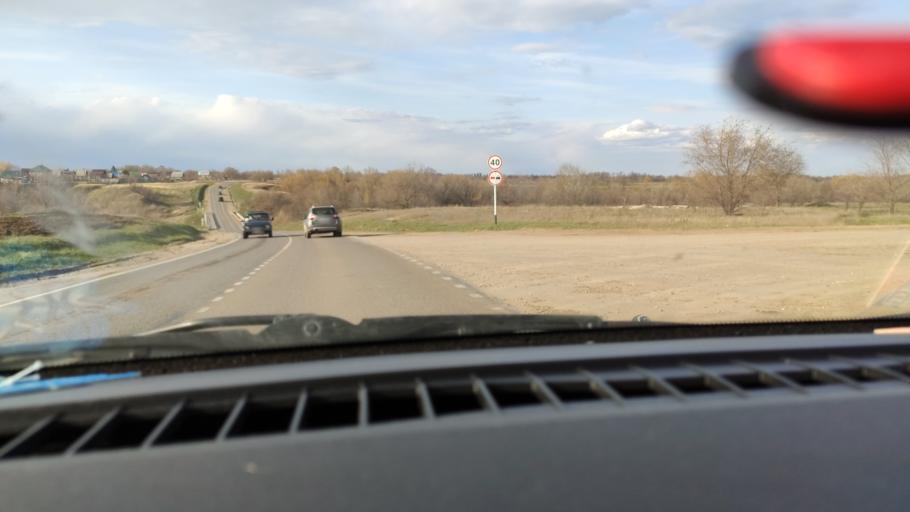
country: RU
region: Saratov
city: Privolzhskiy
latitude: 51.3505
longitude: 46.0445
